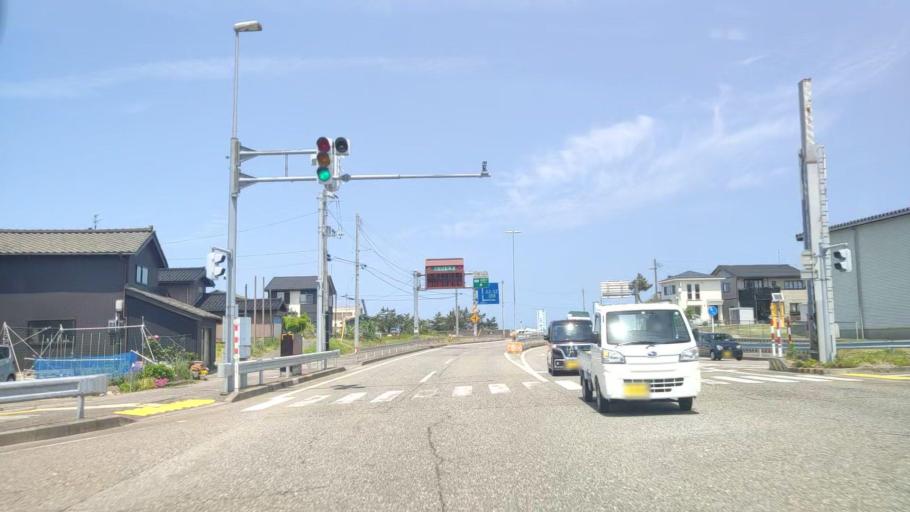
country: JP
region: Niigata
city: Itoigawa
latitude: 37.0421
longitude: 137.8464
